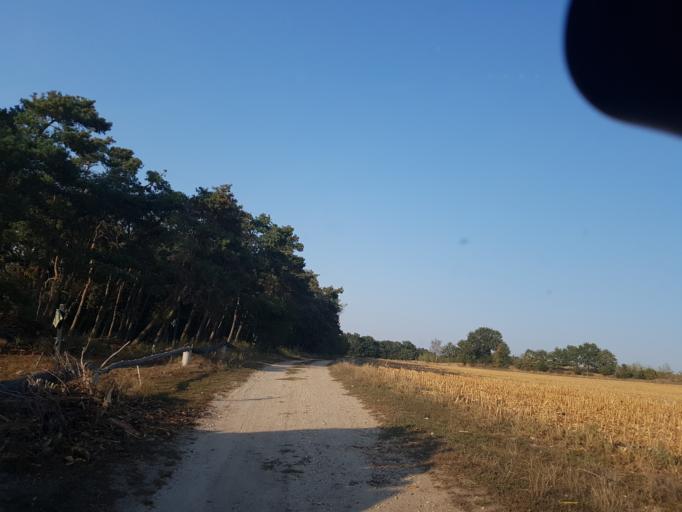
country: DE
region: Saxony
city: Cavertitz
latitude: 51.3866
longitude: 13.1645
